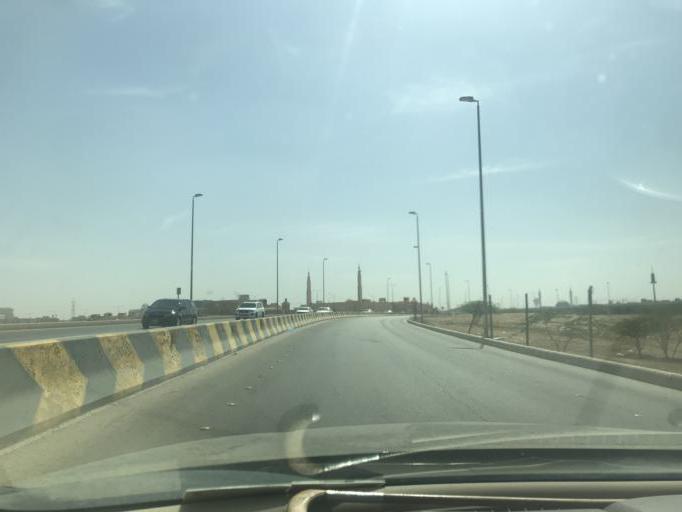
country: SA
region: Ar Riyad
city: Riyadh
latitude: 24.8242
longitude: 46.7208
